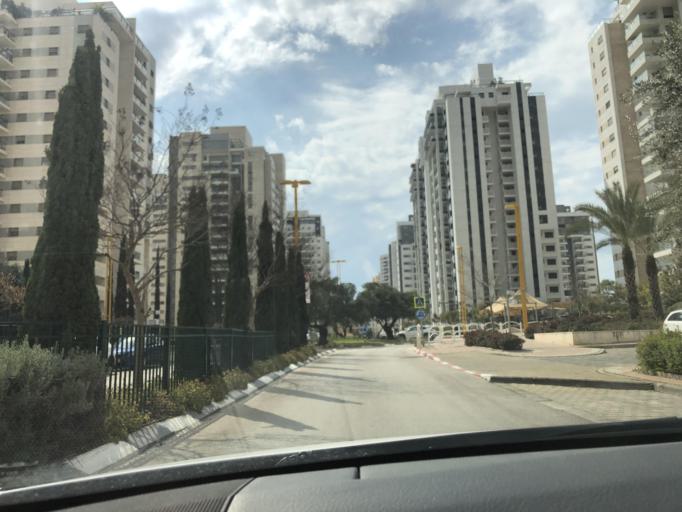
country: IL
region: Central District
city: Ganne Tiqwa
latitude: 32.0647
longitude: 34.8705
